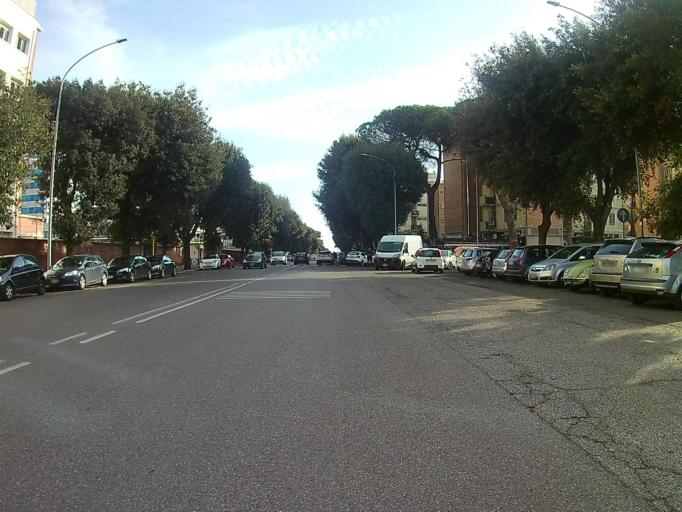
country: IT
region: Latium
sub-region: Citta metropolitana di Roma Capitale
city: Lido di Ostia
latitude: 41.7331
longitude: 12.2927
